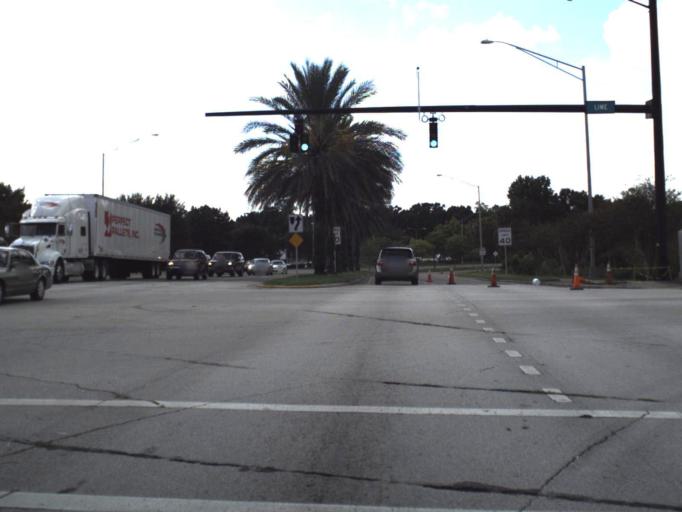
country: US
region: Florida
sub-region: Polk County
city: Lakeland
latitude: 28.0407
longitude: -81.9601
